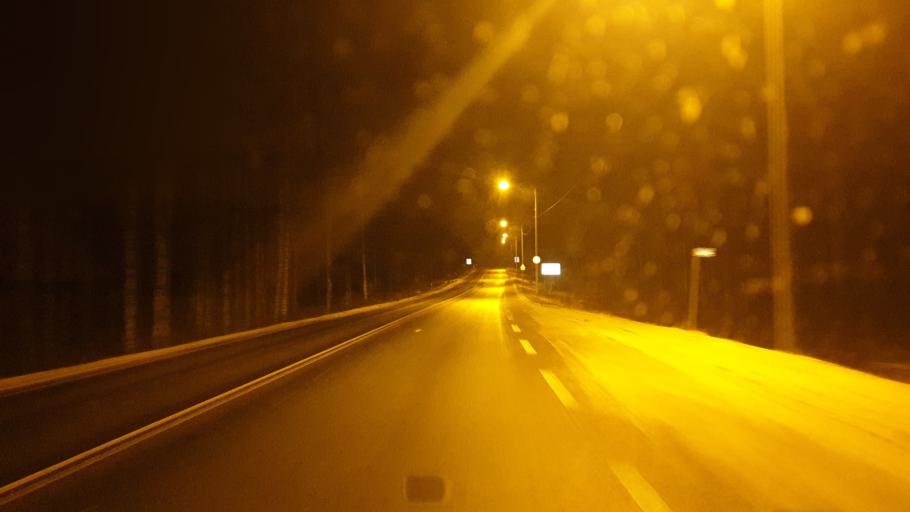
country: FI
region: Central Finland
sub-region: Saarijaervi-Viitasaari
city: Pihtipudas
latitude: 63.2610
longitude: 25.6479
